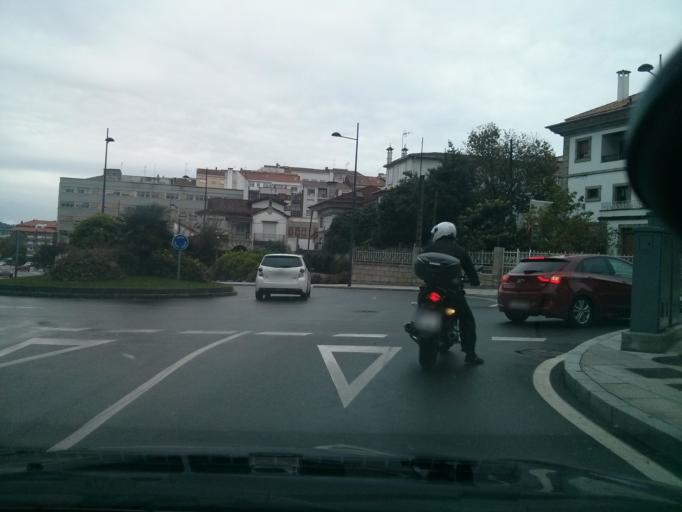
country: ES
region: Galicia
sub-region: Provincia da Coruna
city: Santiago de Compostela
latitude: 42.8719
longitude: -8.5444
